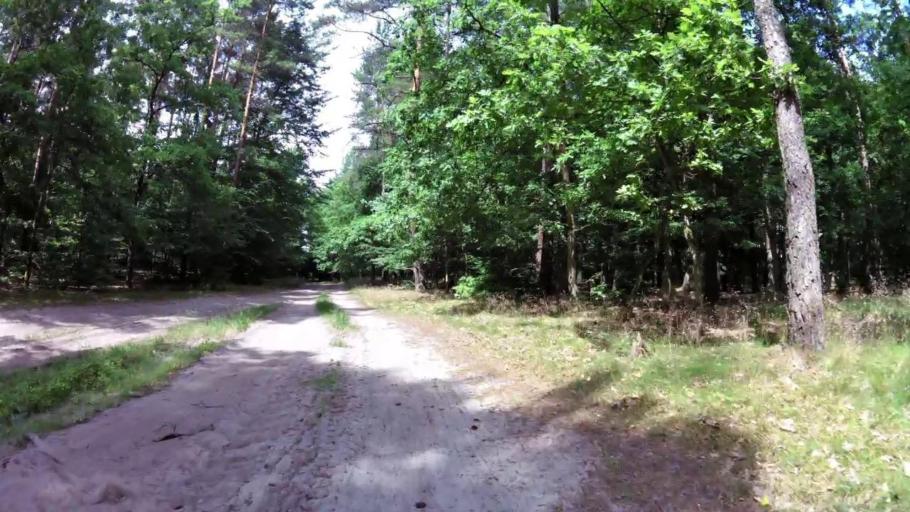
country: PL
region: West Pomeranian Voivodeship
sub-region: Powiat lobeski
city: Lobez
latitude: 53.5986
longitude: 15.6575
